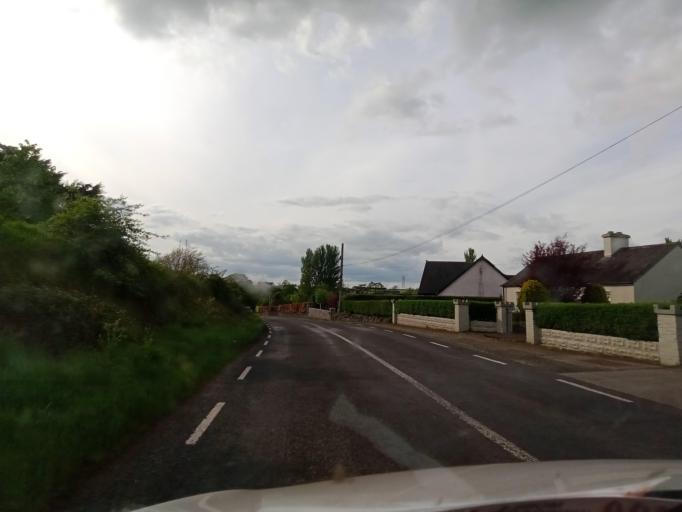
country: IE
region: Leinster
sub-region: Laois
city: Abbeyleix
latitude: 52.9186
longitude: -7.3572
